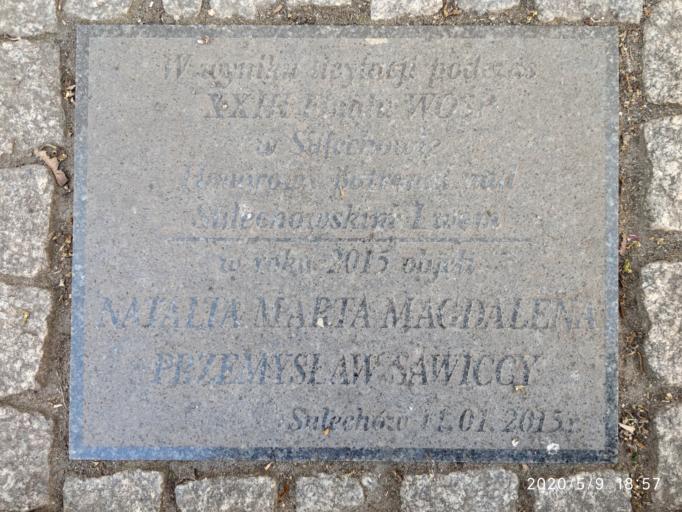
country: PL
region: Lubusz
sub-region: Powiat zielonogorski
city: Sulechow
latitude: 52.0851
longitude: 15.6262
